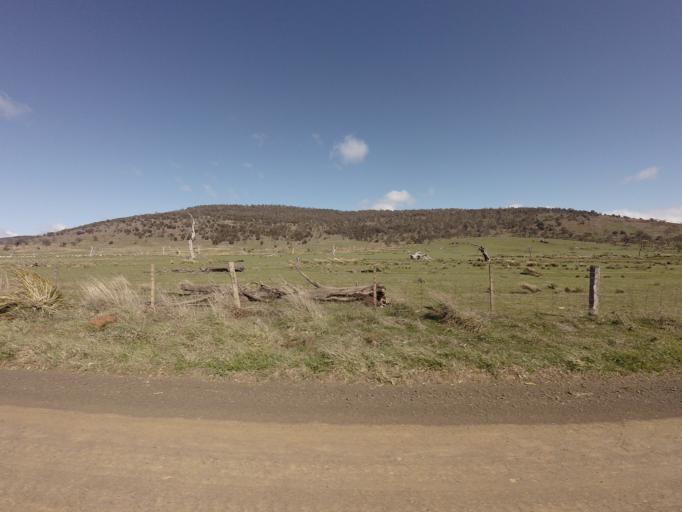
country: AU
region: Tasmania
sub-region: Northern Midlands
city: Evandale
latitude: -41.9243
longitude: 147.4068
